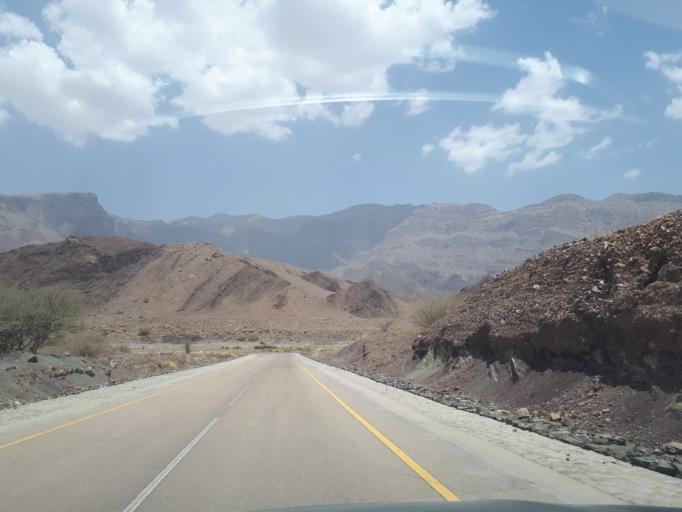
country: OM
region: Ash Sharqiyah
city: Badiyah
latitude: 22.4878
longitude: 59.1271
